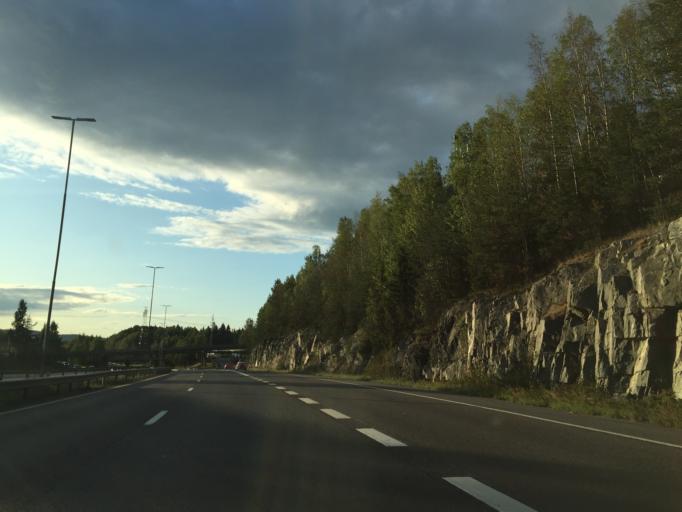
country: NO
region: Akershus
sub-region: Lorenskog
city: Kjenn
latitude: 59.9344
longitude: 10.9406
